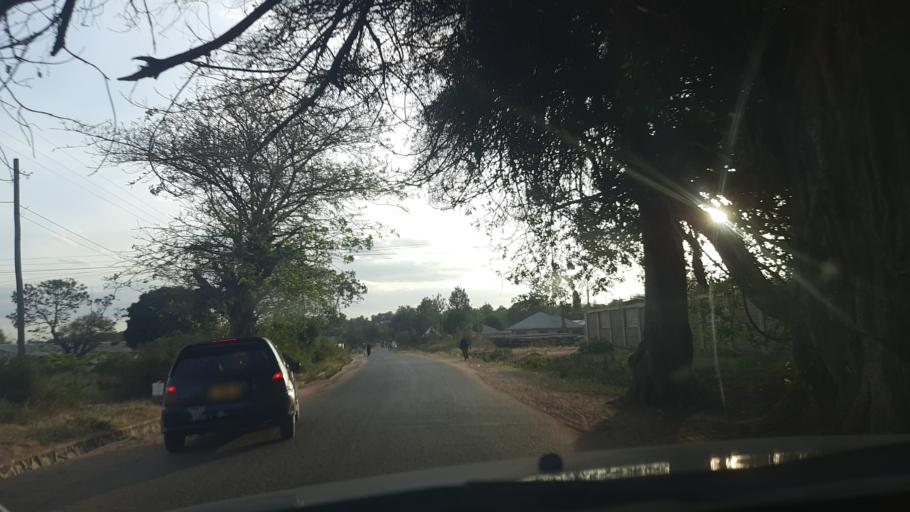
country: TZ
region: Singida
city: Singida
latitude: -4.8111
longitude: 34.7368
